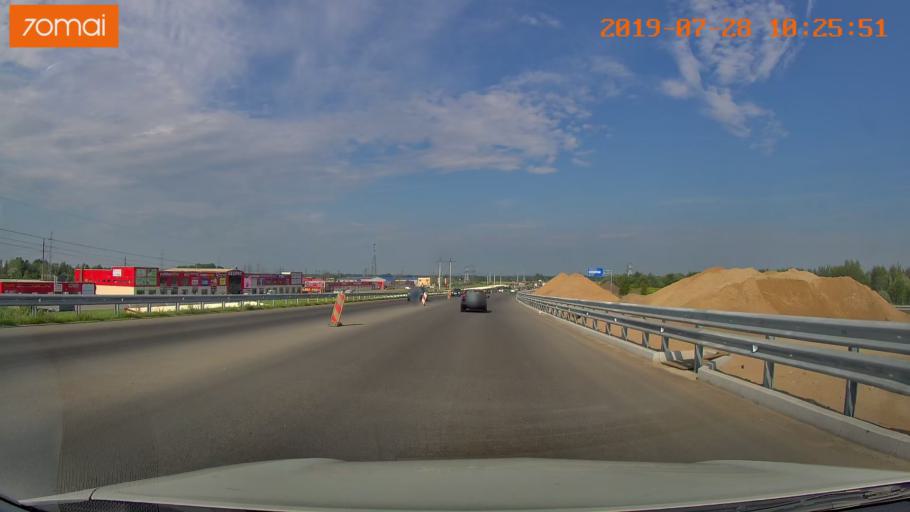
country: RU
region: Kaliningrad
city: Maloye Isakovo
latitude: 54.7680
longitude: 20.5361
